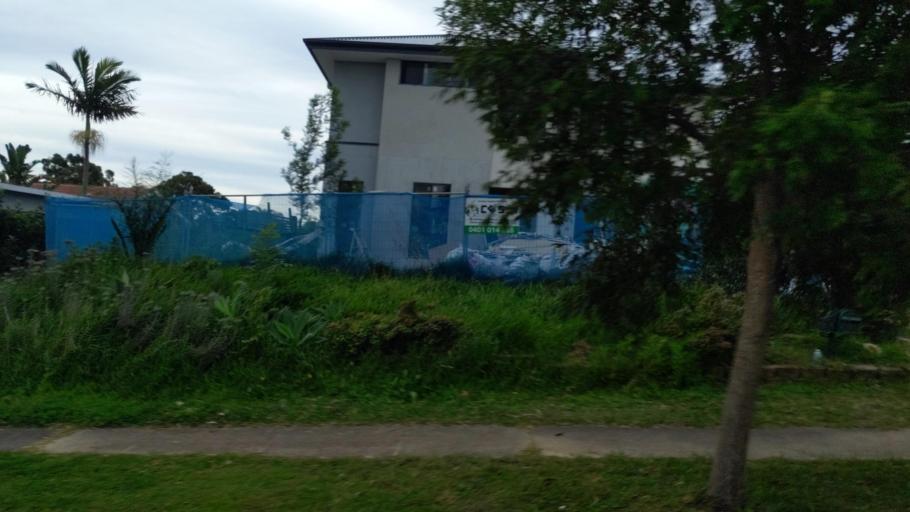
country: AU
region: New South Wales
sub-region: Blacktown
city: Blacktown
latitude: -33.7561
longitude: 150.9503
